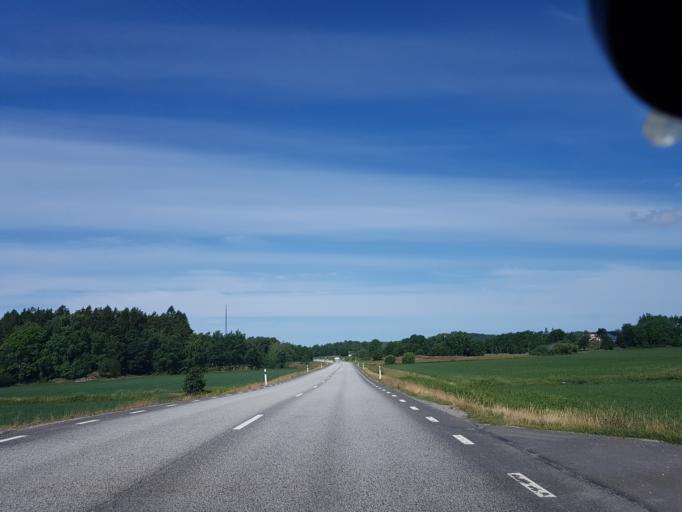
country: SE
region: Vaestra Goetaland
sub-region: Orust
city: Henan
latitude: 58.1525
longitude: 11.5741
